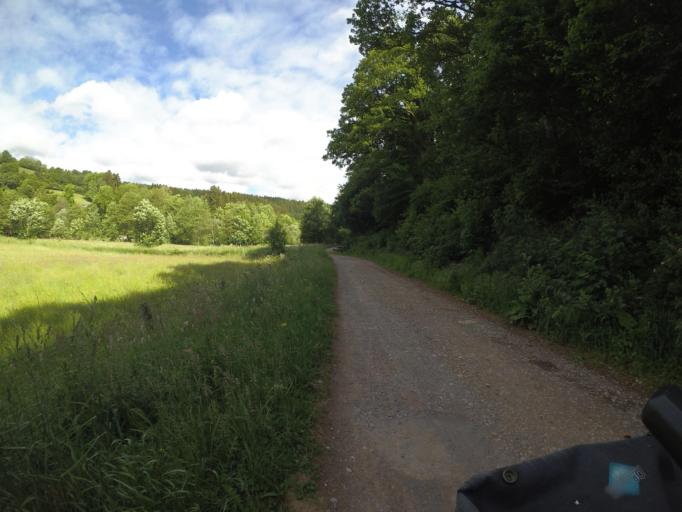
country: DE
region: North Rhine-Westphalia
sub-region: Regierungsbezirk Koln
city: Hellenthal
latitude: 50.4657
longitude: 6.4197
